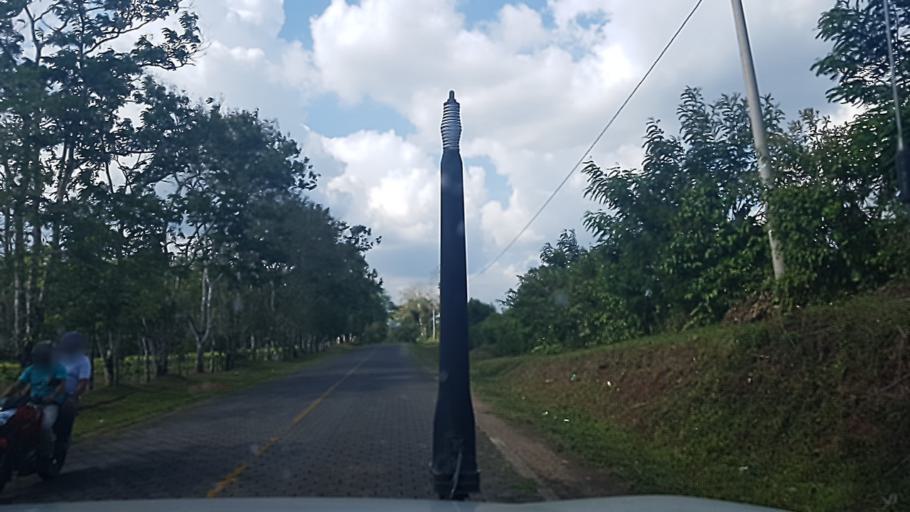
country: NI
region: Atlantico Sur
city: Nueva Guinea
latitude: 11.7005
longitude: -84.3848
